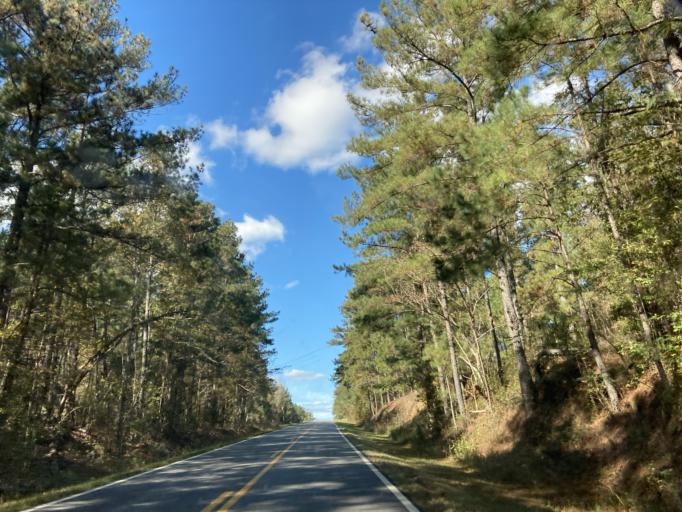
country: US
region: Georgia
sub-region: Jones County
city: Gray
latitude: 32.9351
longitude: -83.5059
